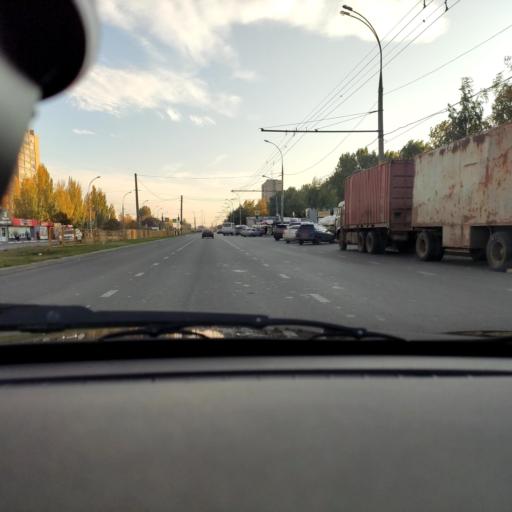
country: RU
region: Samara
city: Tol'yatti
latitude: 53.5094
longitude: 49.2924
